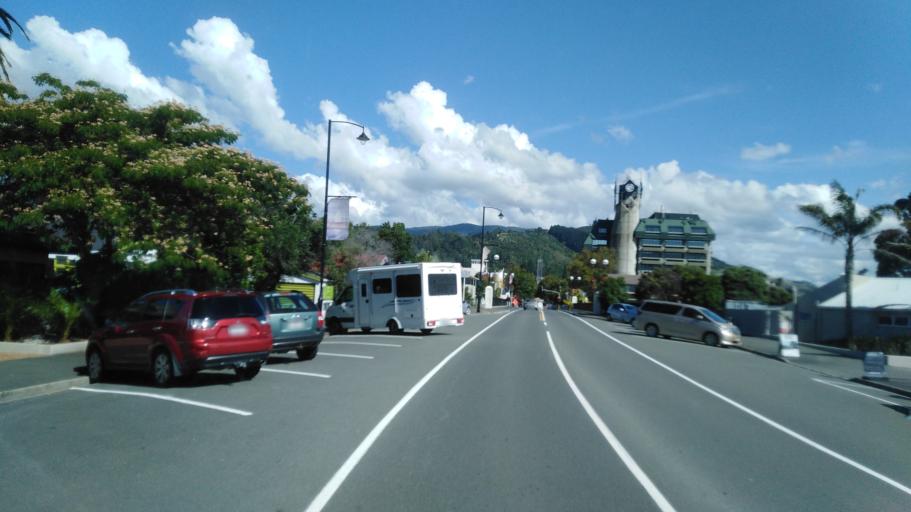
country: NZ
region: Nelson
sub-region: Nelson City
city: Nelson
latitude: -41.2691
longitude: 173.2841
